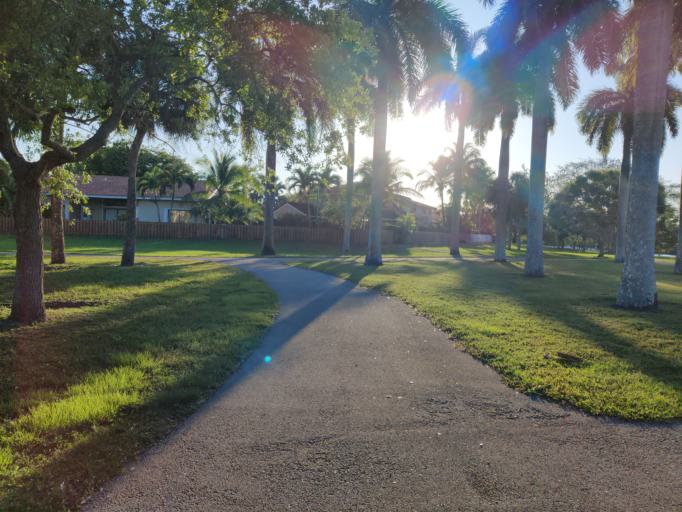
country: US
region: Florida
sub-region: Miami-Dade County
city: The Hammocks
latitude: 25.6672
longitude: -80.4547
